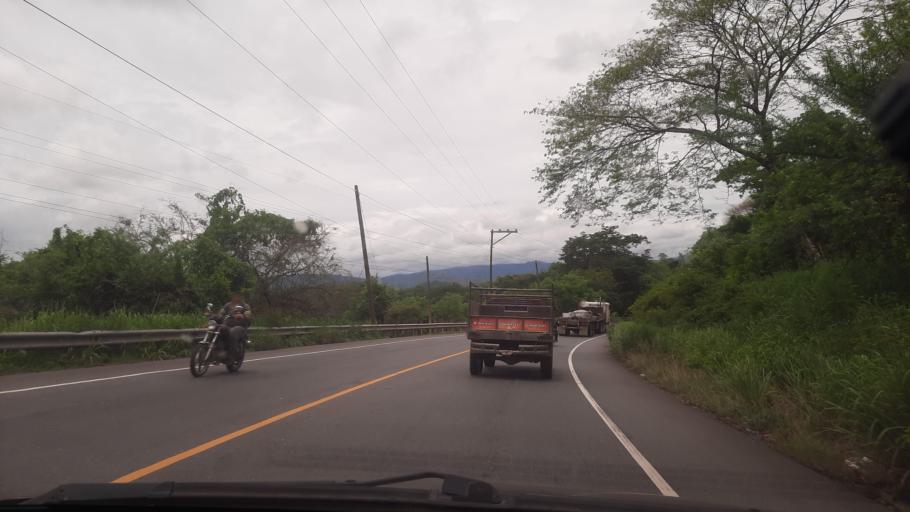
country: GT
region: Zacapa
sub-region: Municipio de Zacapa
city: Gualan
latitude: 15.1513
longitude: -89.3231
